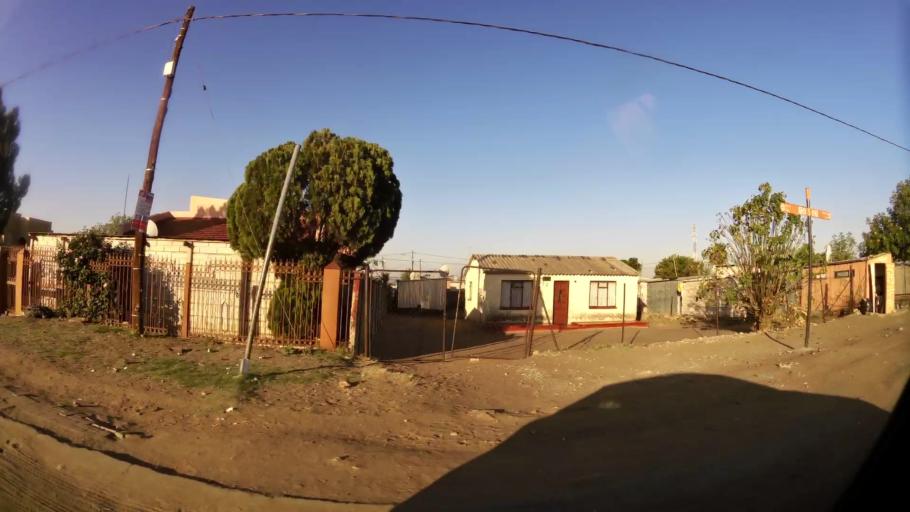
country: ZA
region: North-West
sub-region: Bojanala Platinum District Municipality
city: Rustenburg
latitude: -25.6321
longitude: 27.2155
